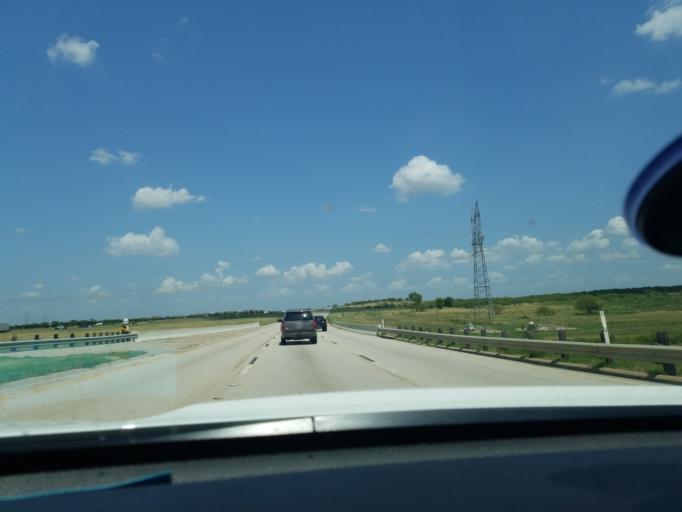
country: US
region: Texas
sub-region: Tarrant County
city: Keller
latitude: 32.9661
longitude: -97.2934
